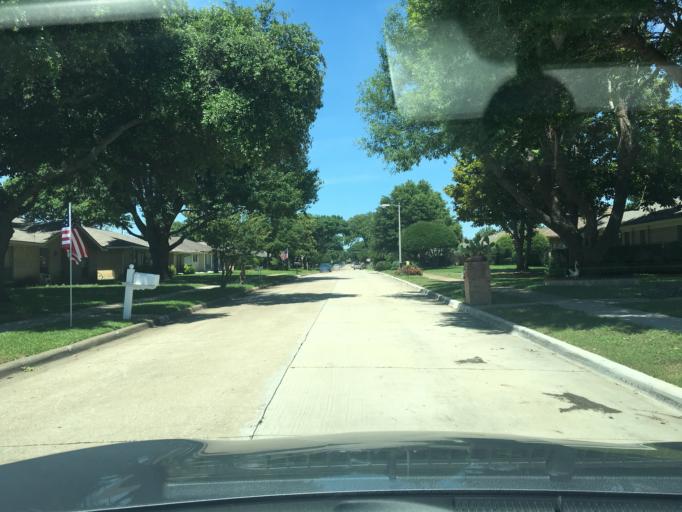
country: US
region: Texas
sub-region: Dallas County
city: Richardson
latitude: 32.9459
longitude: -96.6891
